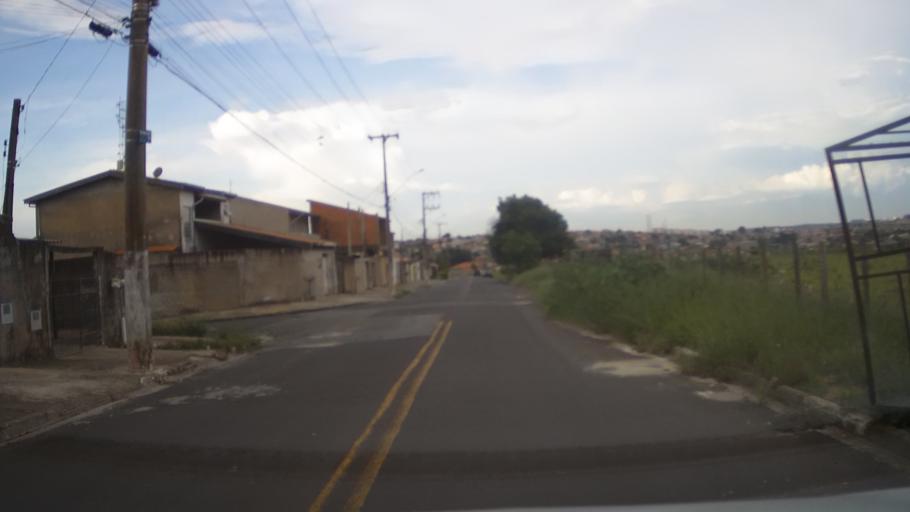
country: BR
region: Sao Paulo
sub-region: Hortolandia
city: Hortolandia
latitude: -22.9640
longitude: -47.1893
